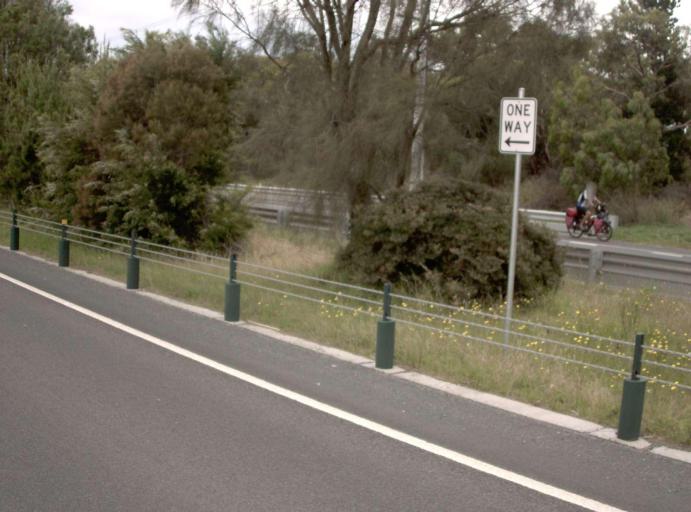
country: AU
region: Victoria
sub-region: Casey
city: Cranbourne East
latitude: -38.1243
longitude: 145.2894
